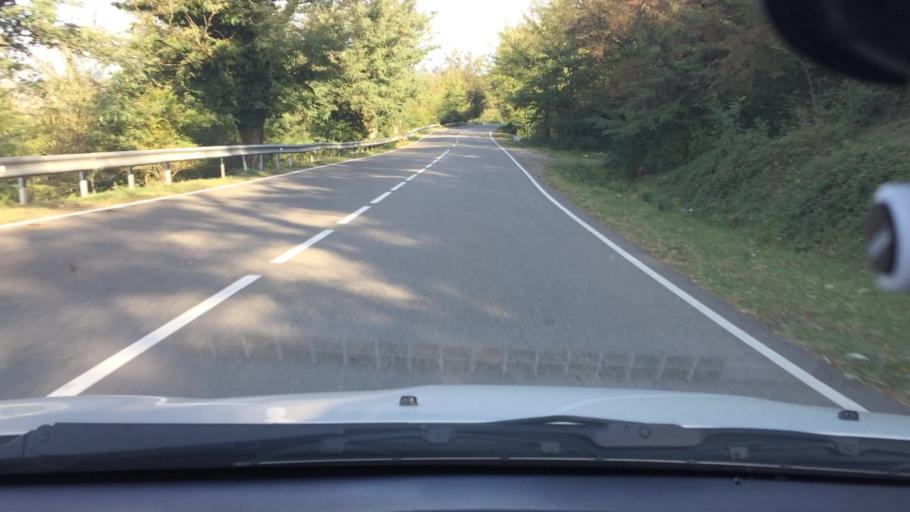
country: GE
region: Imereti
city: Kutaisi
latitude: 42.2525
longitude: 42.7498
